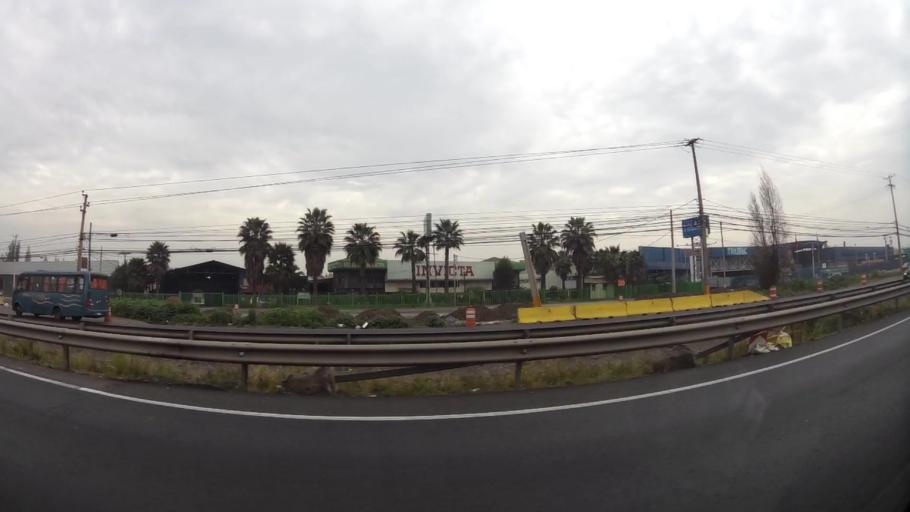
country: CL
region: Santiago Metropolitan
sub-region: Provincia de Chacabuco
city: Chicureo Abajo
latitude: -33.2813
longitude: -70.7384
